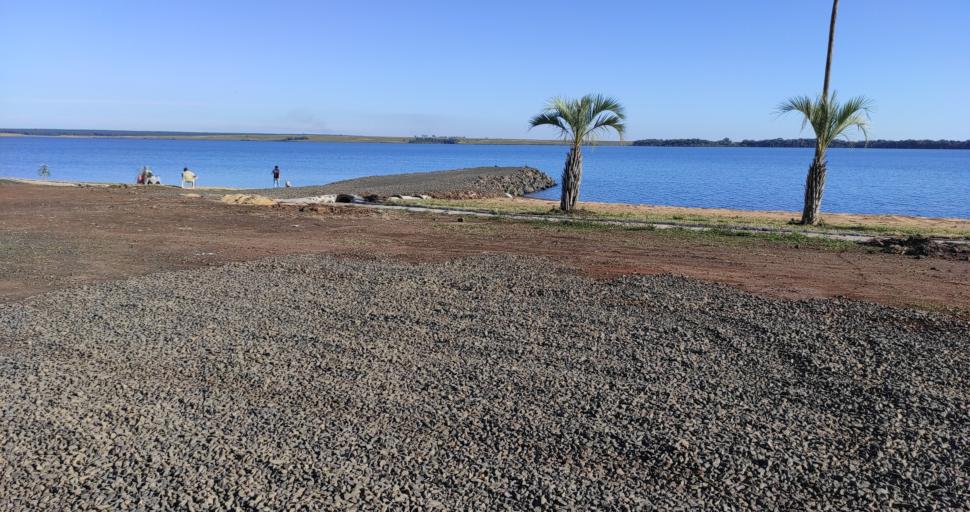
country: PY
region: Itapua
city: Carmen del Parana
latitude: -27.4110
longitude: -56.1853
